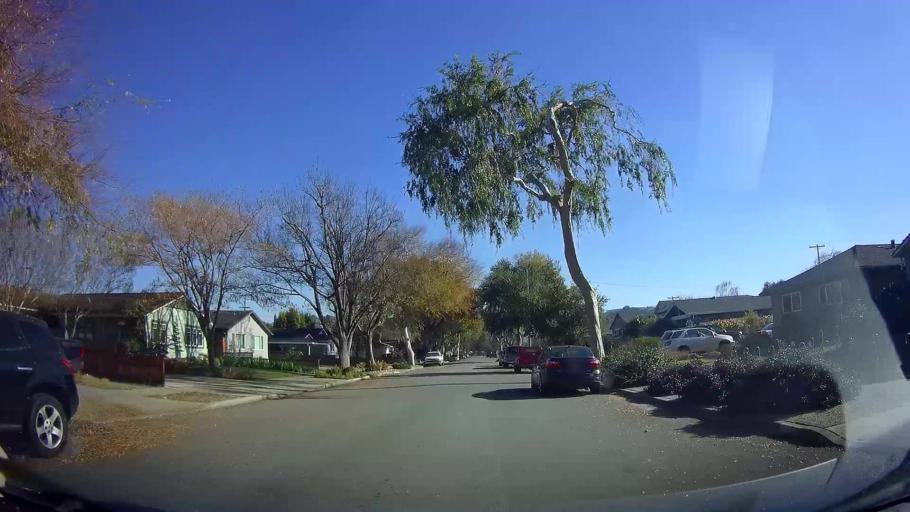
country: US
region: California
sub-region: Santa Clara County
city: Seven Trees
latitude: 37.2877
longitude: -121.8800
